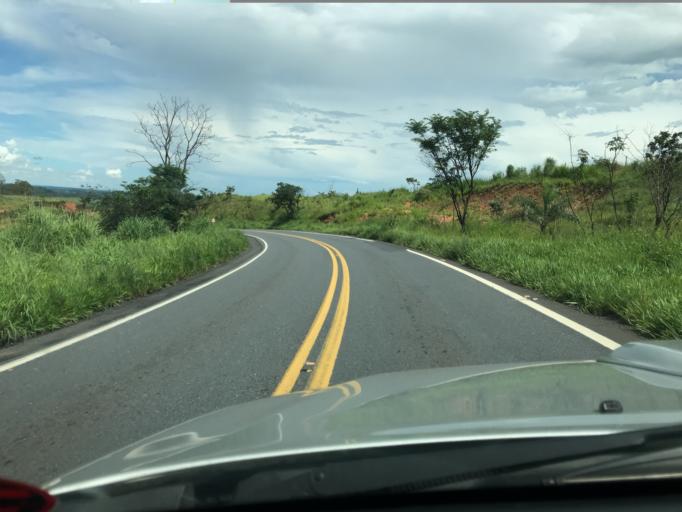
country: BR
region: Minas Gerais
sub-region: Campos Altos
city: Campos Altos
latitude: -19.7944
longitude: -46.0374
